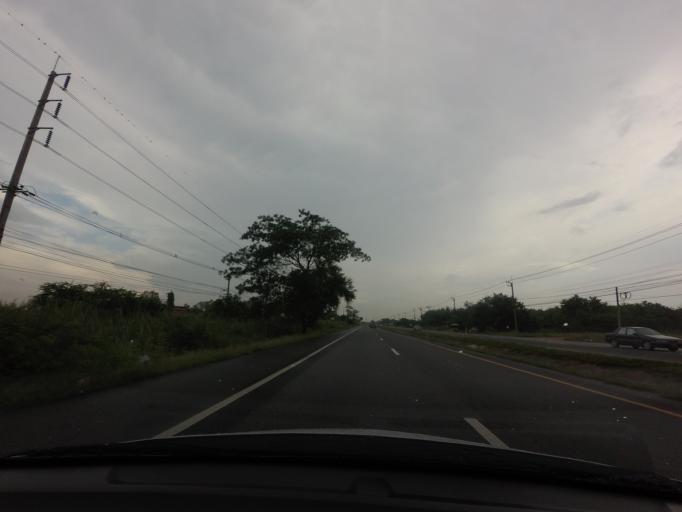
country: TH
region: Bangkok
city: Nong Chok
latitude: 13.8105
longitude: 100.9167
